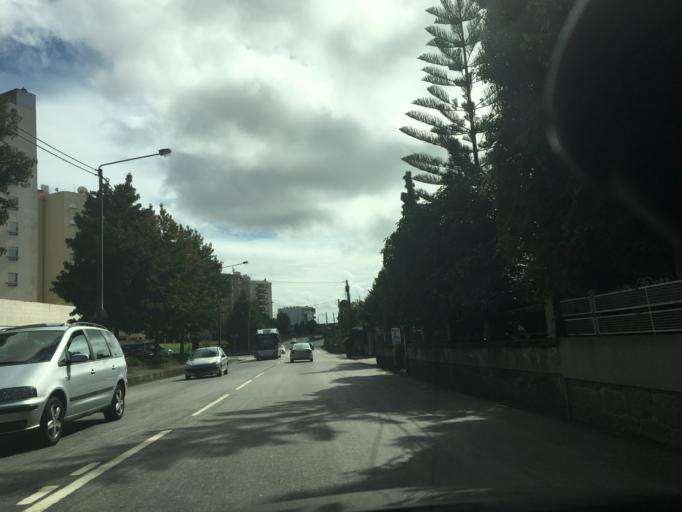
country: PT
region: Porto
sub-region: Maia
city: Gemunde
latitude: 41.2514
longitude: -8.6512
